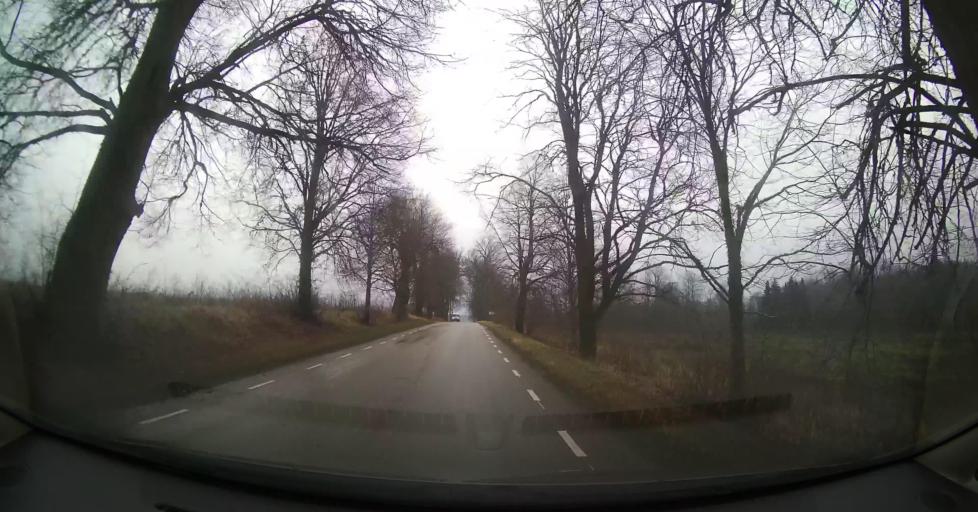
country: EE
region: Tartu
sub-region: Tartu linn
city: Tartu
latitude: 58.3839
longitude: 27.0207
